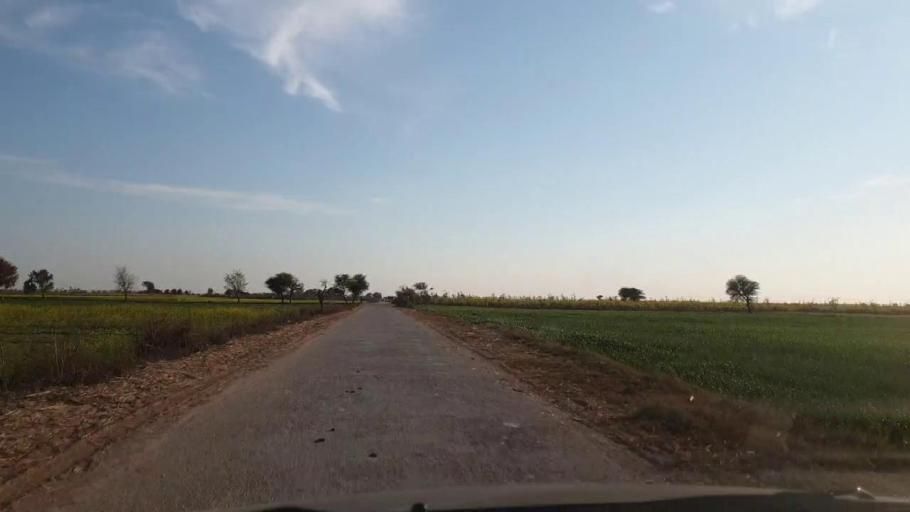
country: PK
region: Sindh
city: Khadro
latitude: 26.1771
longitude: 68.7528
